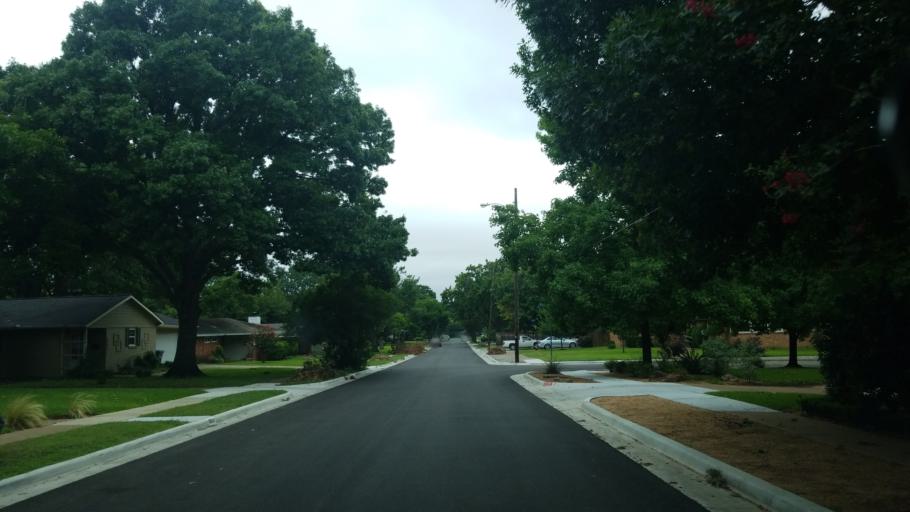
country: US
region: Texas
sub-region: Dallas County
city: Farmers Branch
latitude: 32.8837
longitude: -96.8569
